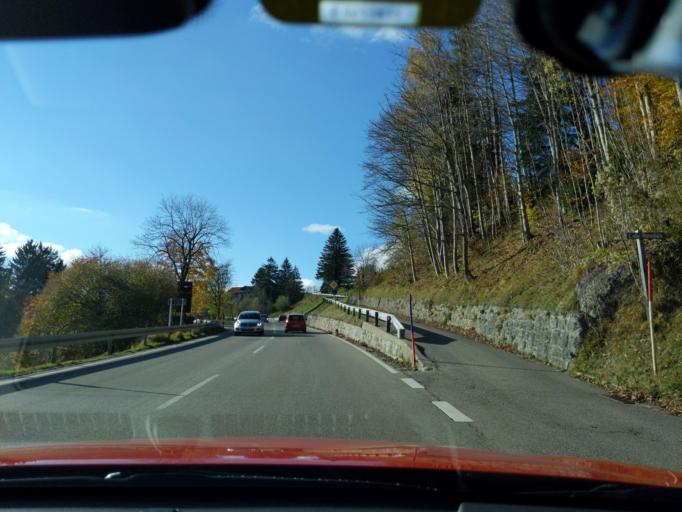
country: DE
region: Bavaria
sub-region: Swabia
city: Oberstaufen
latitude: 47.5467
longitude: 9.9998
